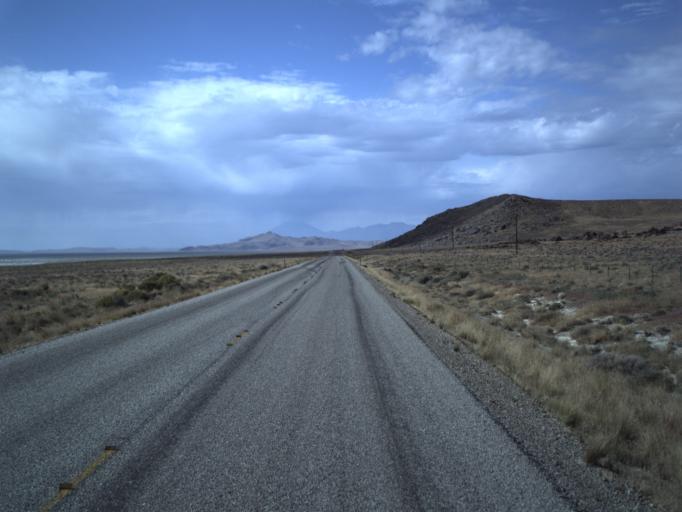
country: US
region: Utah
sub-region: Tooele County
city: Wendover
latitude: 41.4646
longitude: -113.6475
